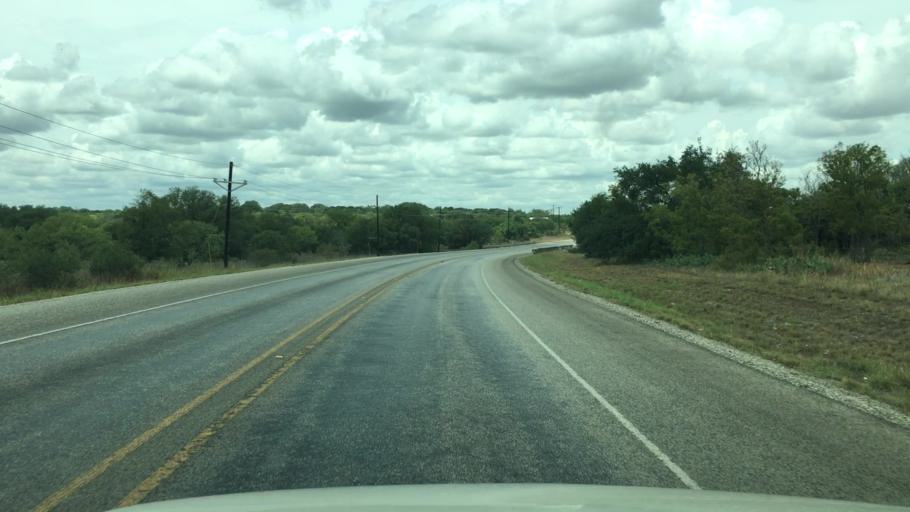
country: US
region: Texas
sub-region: McCulloch County
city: Brady
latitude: 31.0046
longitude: -99.2007
